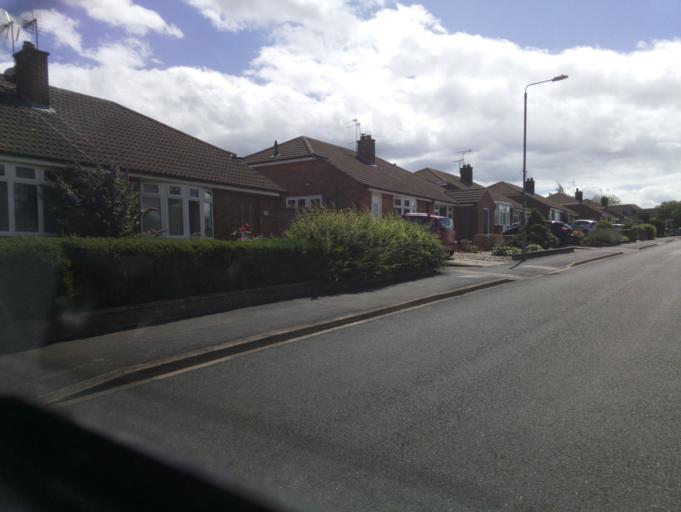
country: GB
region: England
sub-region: Nottinghamshire
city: Cotgrave
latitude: 52.8718
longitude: -1.0829
